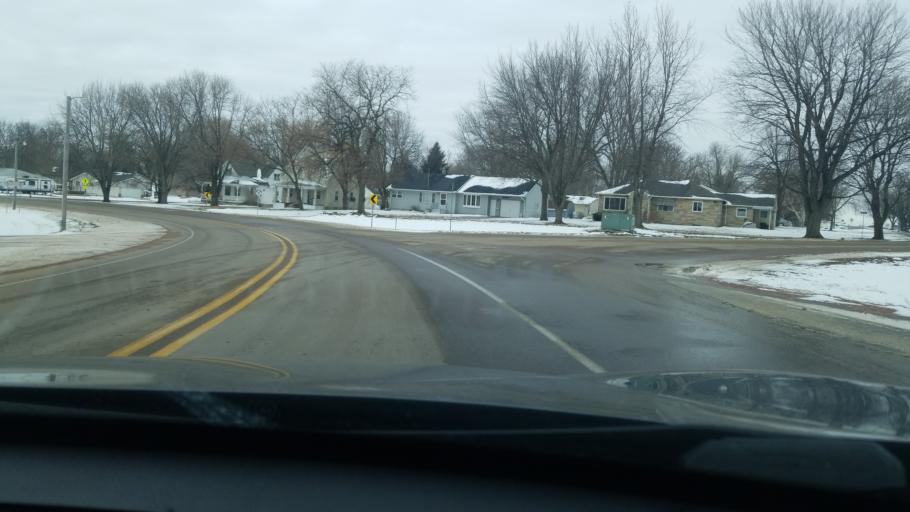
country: US
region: South Dakota
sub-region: Minnehaha County
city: Brandon
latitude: 43.4524
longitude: -96.4298
